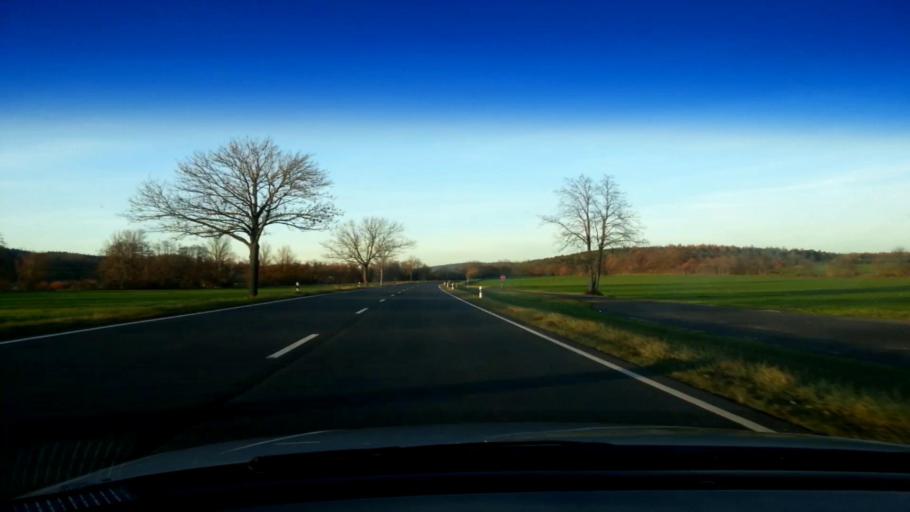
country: DE
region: Bavaria
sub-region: Upper Franconia
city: Rattelsdorf
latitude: 50.0274
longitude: 10.8821
